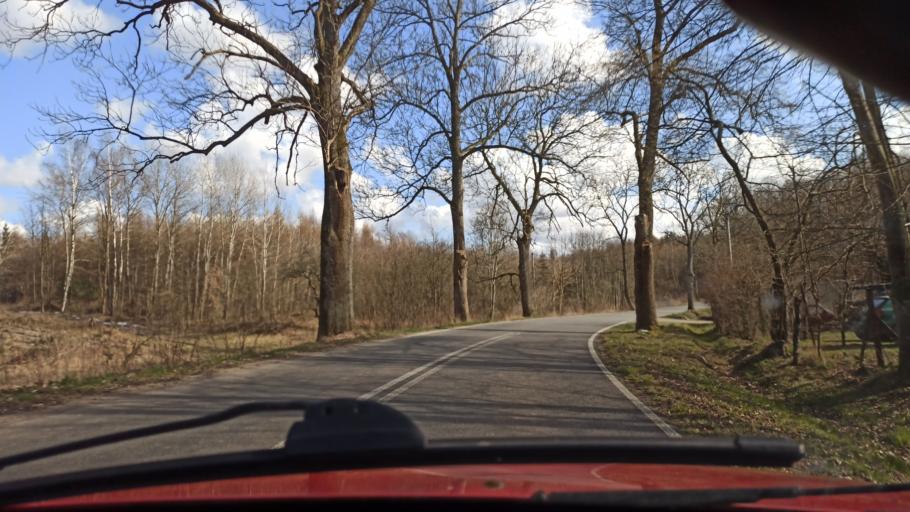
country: PL
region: Warmian-Masurian Voivodeship
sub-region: Powiat elblaski
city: Tolkmicko
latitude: 54.2794
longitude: 19.4804
